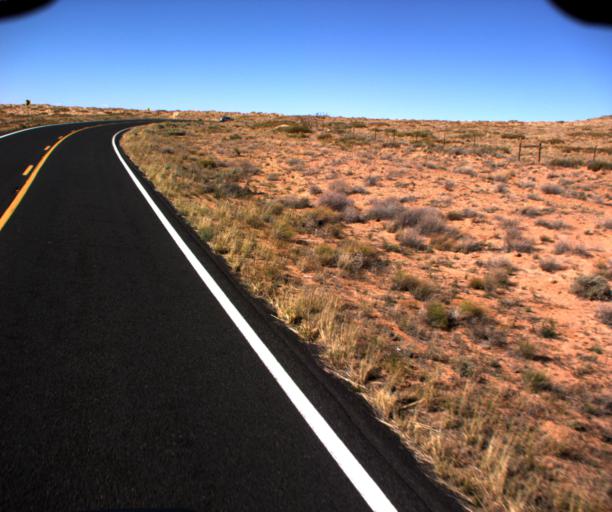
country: US
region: Arizona
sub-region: Coconino County
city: Tuba City
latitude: 36.0359
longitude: -111.1831
